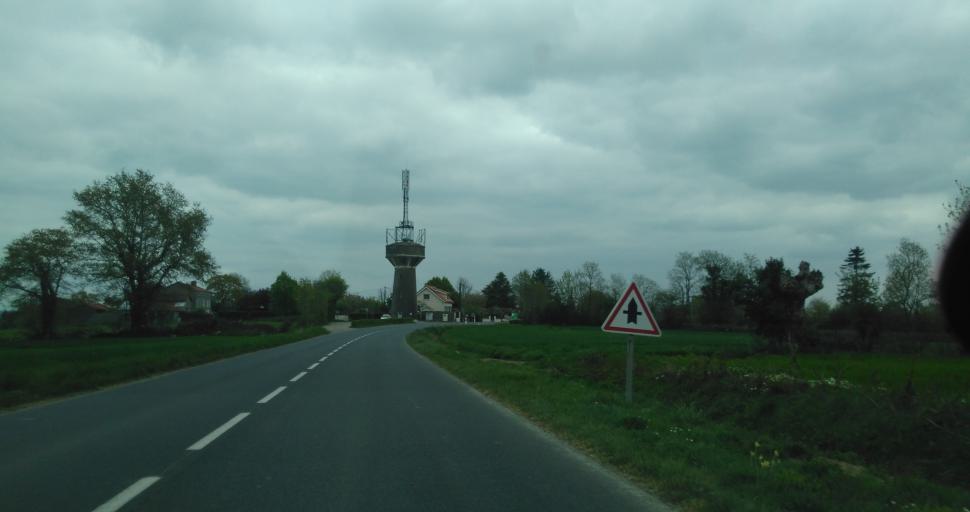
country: FR
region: Poitou-Charentes
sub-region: Departement des Deux-Sevres
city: La Chapelle-Saint-Laurent
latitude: 46.7369
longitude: -0.4844
